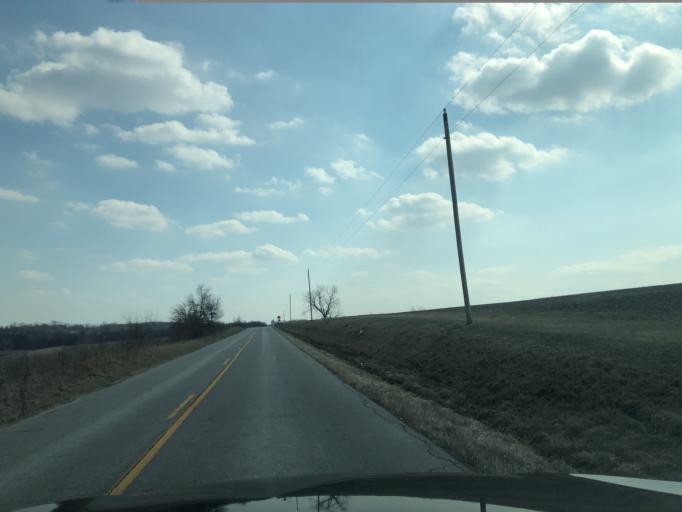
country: US
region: Missouri
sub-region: Platte County
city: Weston
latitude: 39.4940
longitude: -94.8454
